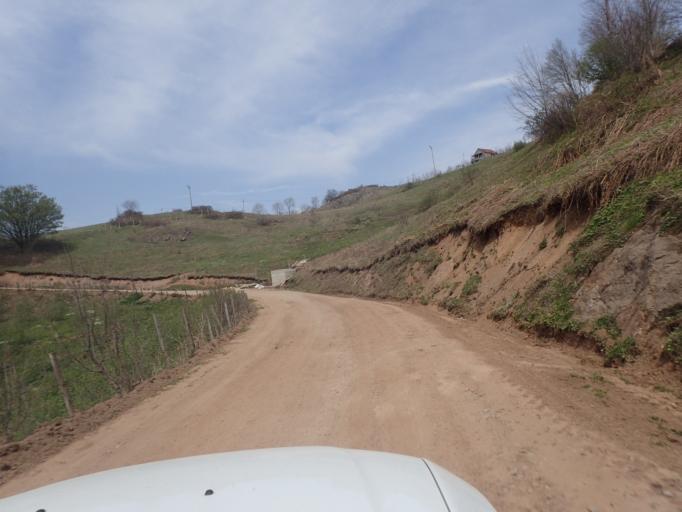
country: TR
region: Ordu
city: Aybasti
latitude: 40.7032
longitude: 37.2908
